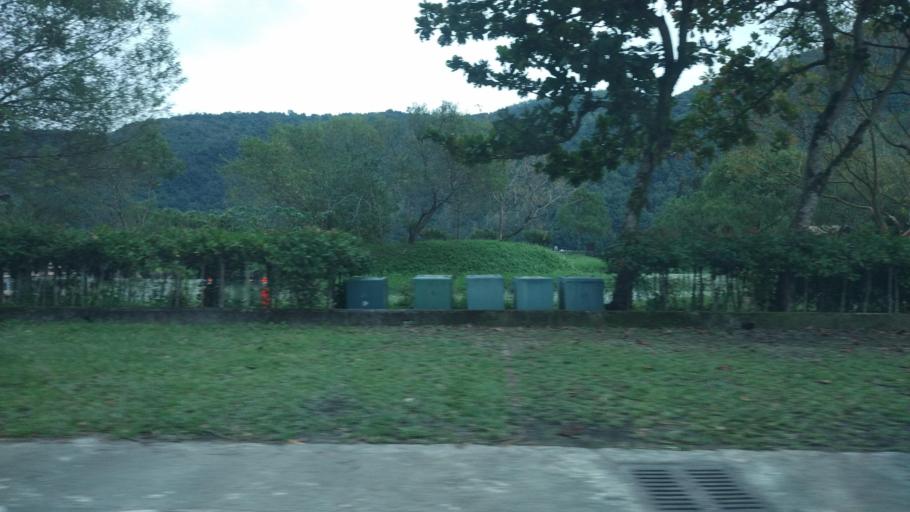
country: TW
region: Taiwan
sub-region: Hualien
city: Hualian
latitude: 23.9255
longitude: 121.5056
